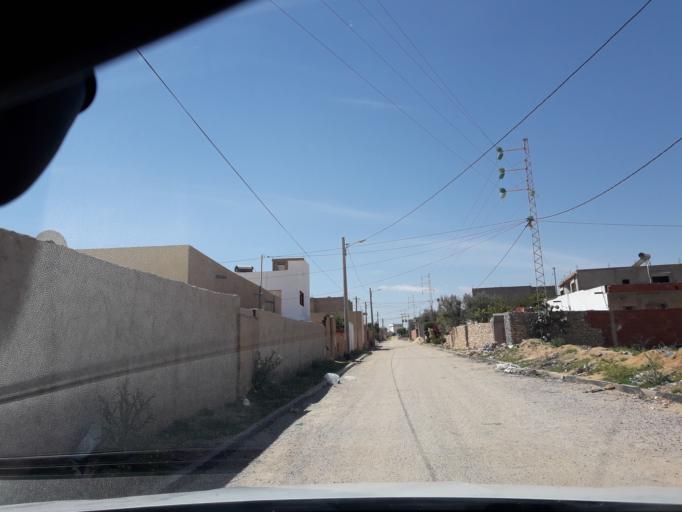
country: TN
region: Safaqis
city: Sfax
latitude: 34.7469
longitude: 10.5125
